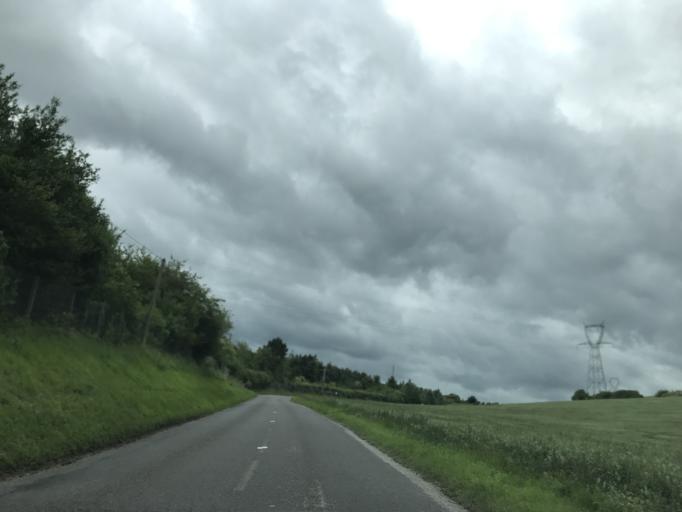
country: FR
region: Haute-Normandie
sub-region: Departement de l'Eure
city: Garennes-sur-Eure
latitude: 48.9007
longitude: 1.4285
